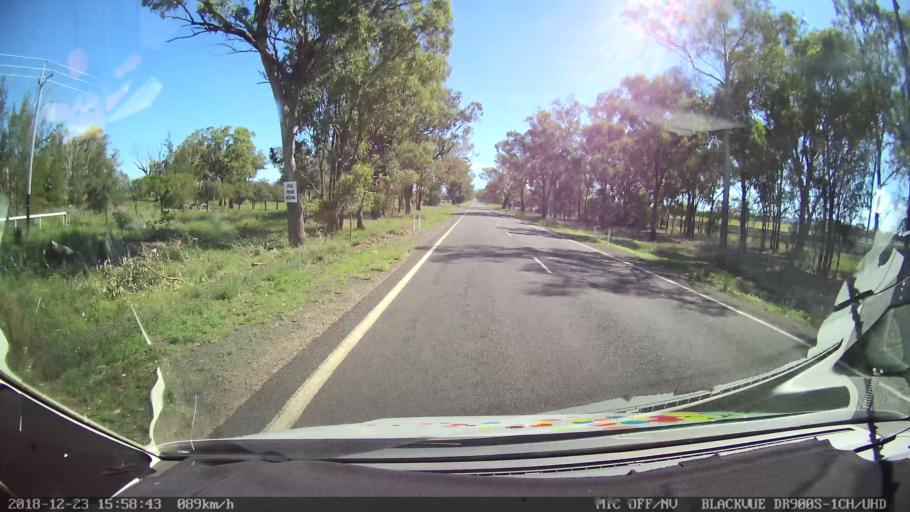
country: AU
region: New South Wales
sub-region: Tamworth Municipality
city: Phillip
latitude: -31.1914
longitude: 150.8394
